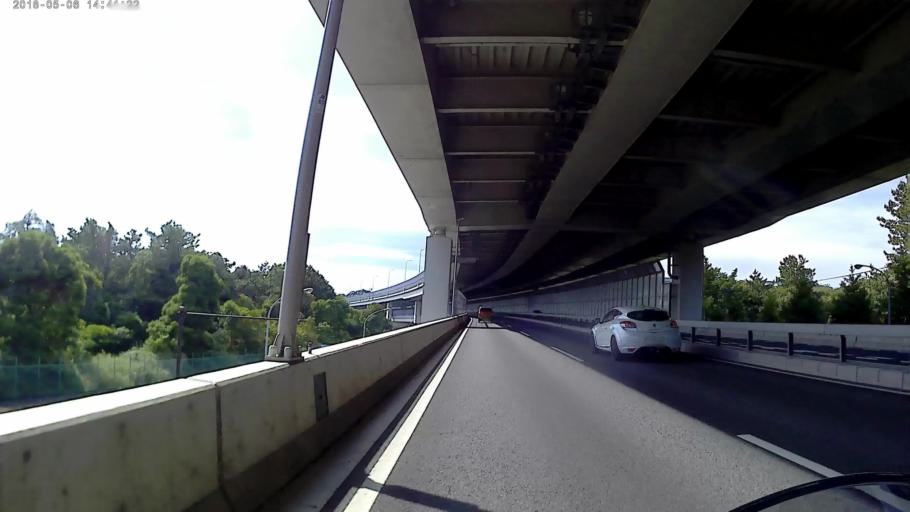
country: JP
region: Kanagawa
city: Yokohama
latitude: 35.4159
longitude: 139.6550
